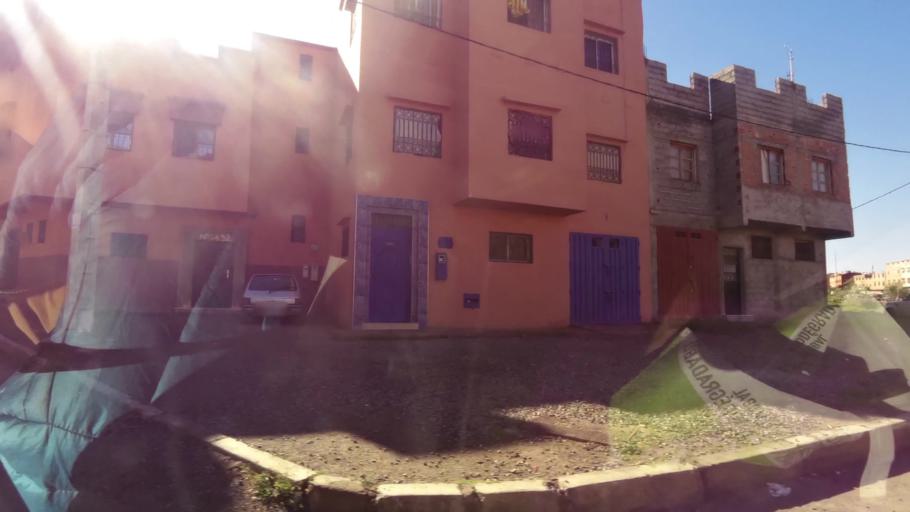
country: MA
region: Marrakech-Tensift-Al Haouz
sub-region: Marrakech
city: Marrakesh
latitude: 31.6008
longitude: -8.0371
